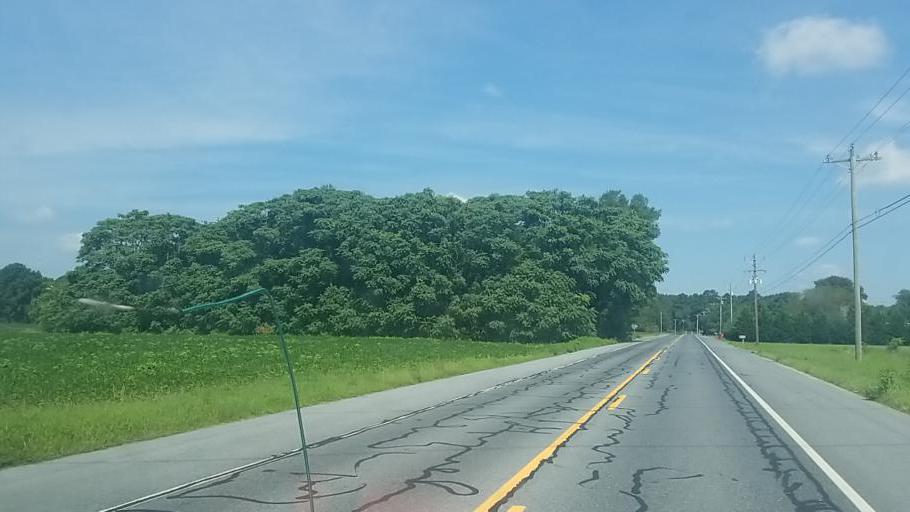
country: US
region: Delaware
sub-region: Sussex County
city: Seaford
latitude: 38.6718
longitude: -75.5739
